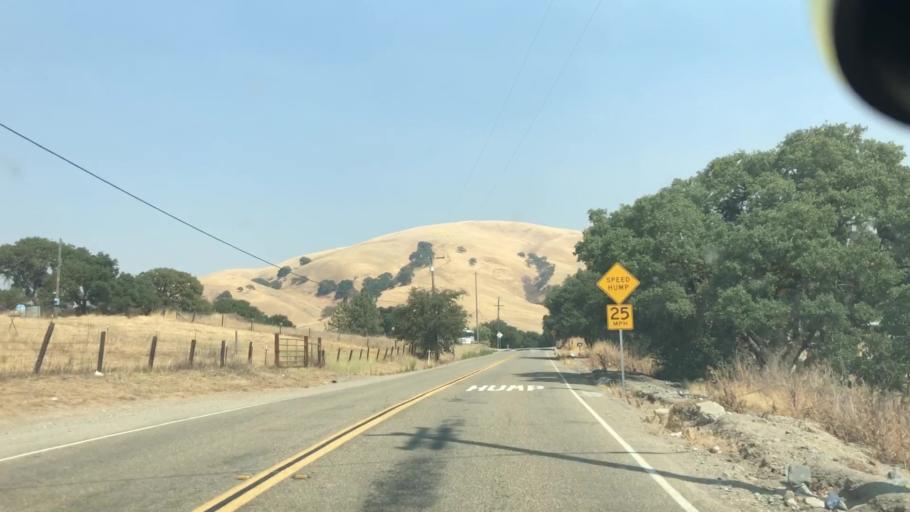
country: US
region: California
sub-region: Alameda County
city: Livermore
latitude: 37.6429
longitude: -121.6438
